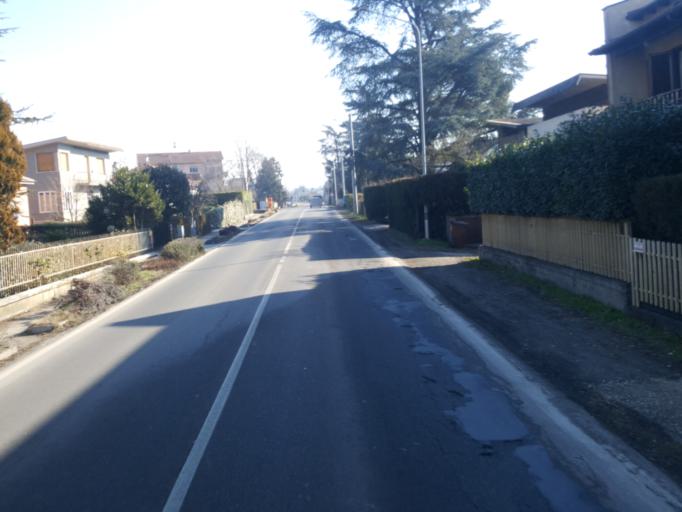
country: IT
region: Piedmont
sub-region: Provincia di Alessandria
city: Viguzzolo
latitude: 44.9057
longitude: 8.9258
